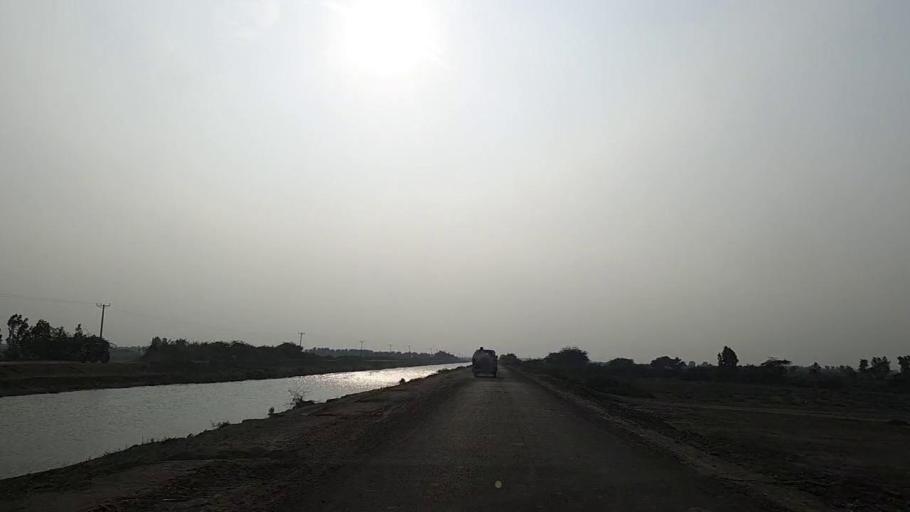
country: PK
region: Sindh
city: Mirpur Sakro
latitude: 24.6366
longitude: 67.5891
